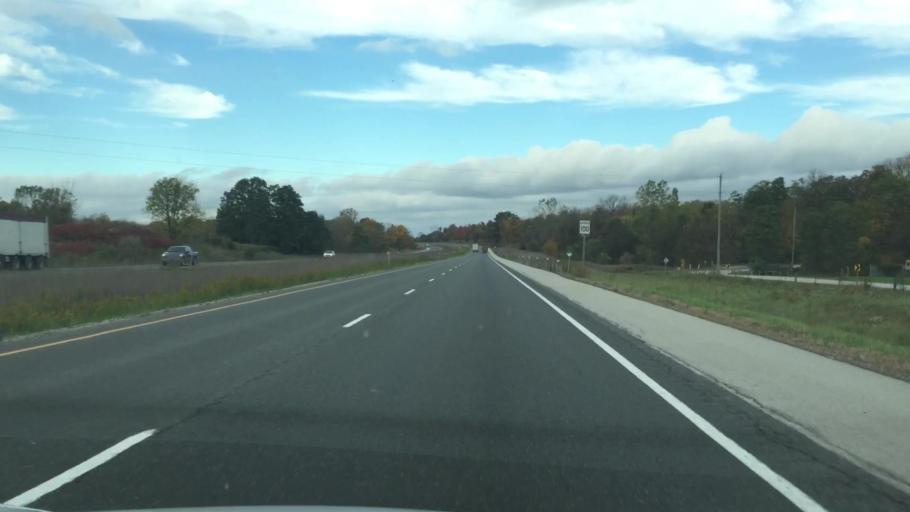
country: CA
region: Ontario
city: Delaware
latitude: 42.8951
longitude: -81.3686
